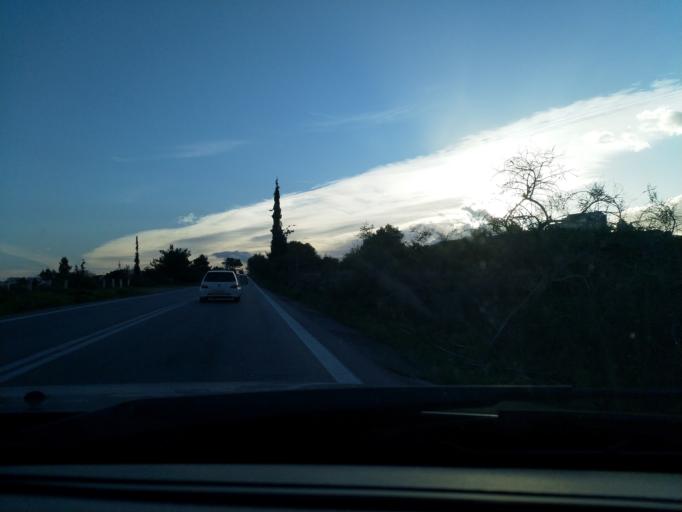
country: GR
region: Crete
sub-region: Nomos Chanias
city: Pithari
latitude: 35.5208
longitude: 24.0639
